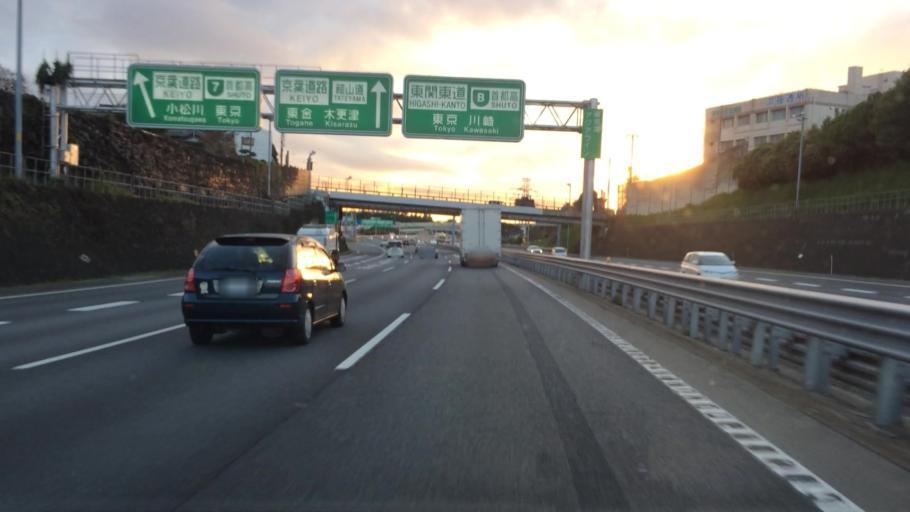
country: JP
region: Chiba
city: Yotsukaido
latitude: 35.6689
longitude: 140.1141
